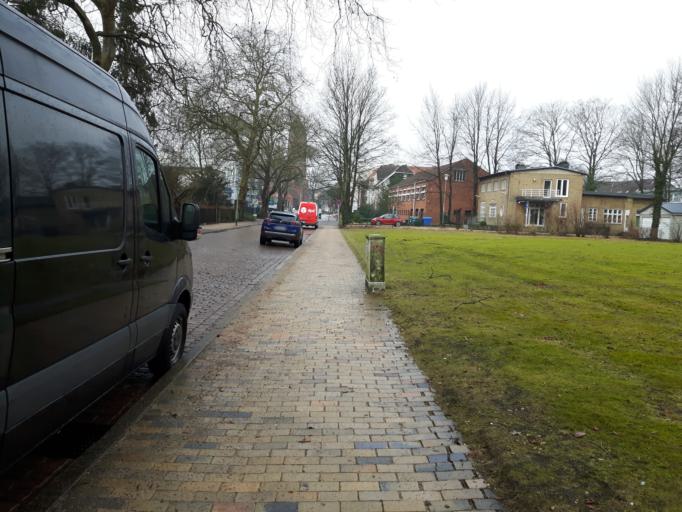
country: DE
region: Schleswig-Holstein
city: Neumunster
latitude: 54.0750
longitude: 9.9892
